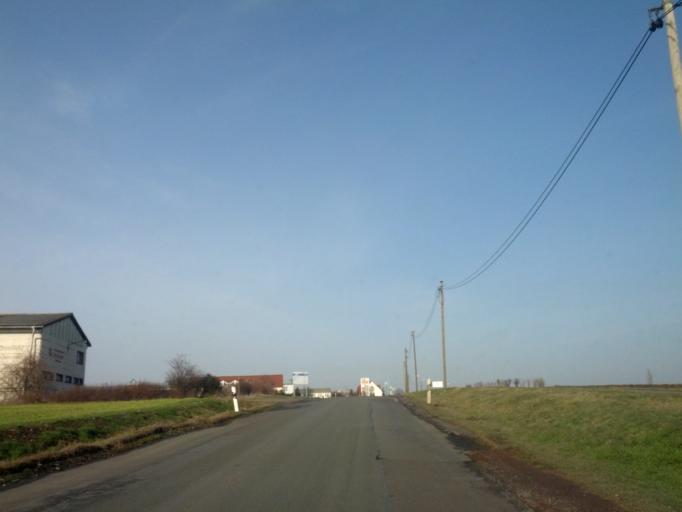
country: DE
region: Thuringia
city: Wandersleben
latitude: 50.8887
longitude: 10.8478
